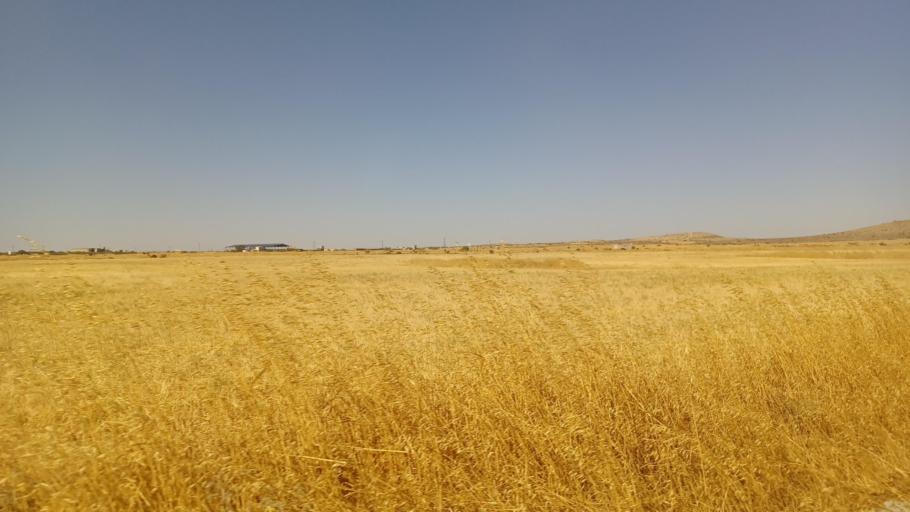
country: CY
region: Larnaka
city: Pergamos
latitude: 35.0407
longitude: 33.6875
